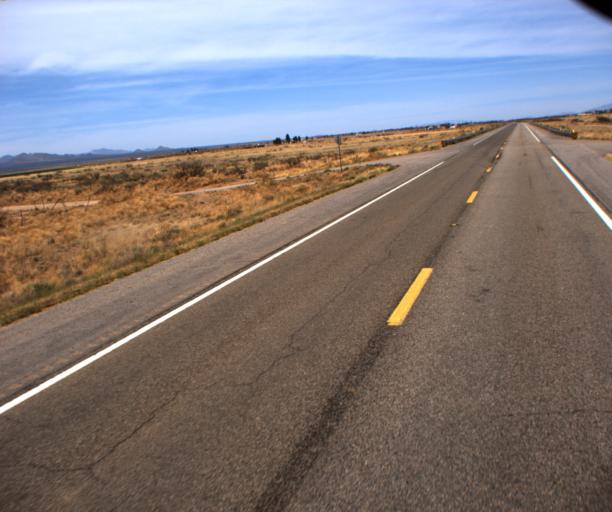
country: US
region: Arizona
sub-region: Cochise County
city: Pirtleville
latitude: 31.6412
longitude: -109.6725
